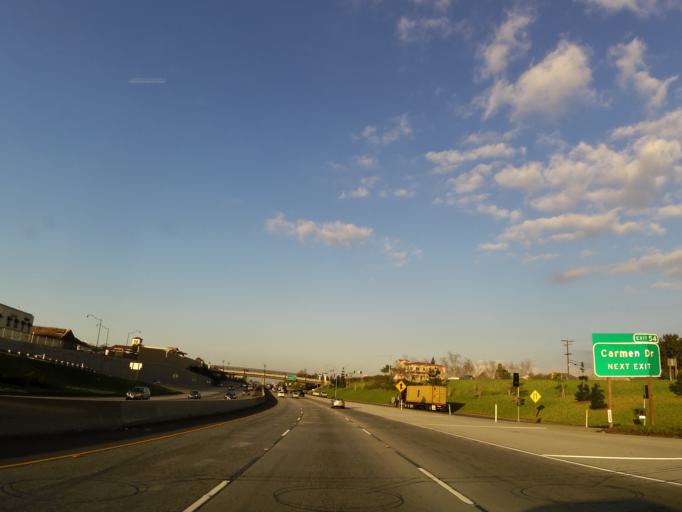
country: US
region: California
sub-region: Ventura County
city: Camarillo
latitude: 34.2171
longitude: -119.0358
